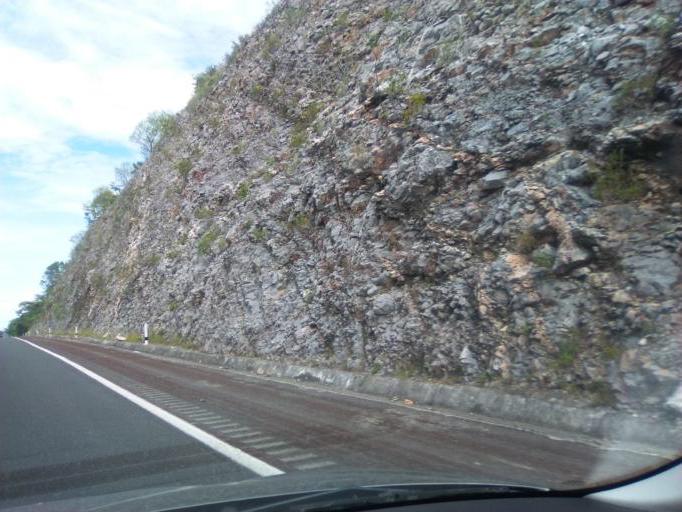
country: MX
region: Guerrero
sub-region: Eduardo Neri
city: Axaxacualco
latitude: 17.8127
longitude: -99.4626
